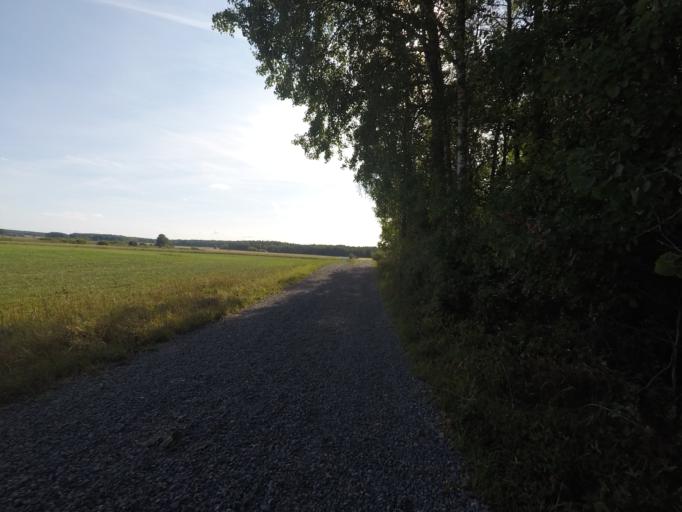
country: SE
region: Soedermanland
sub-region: Eskilstuna Kommun
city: Kvicksund
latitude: 59.4395
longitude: 16.2687
